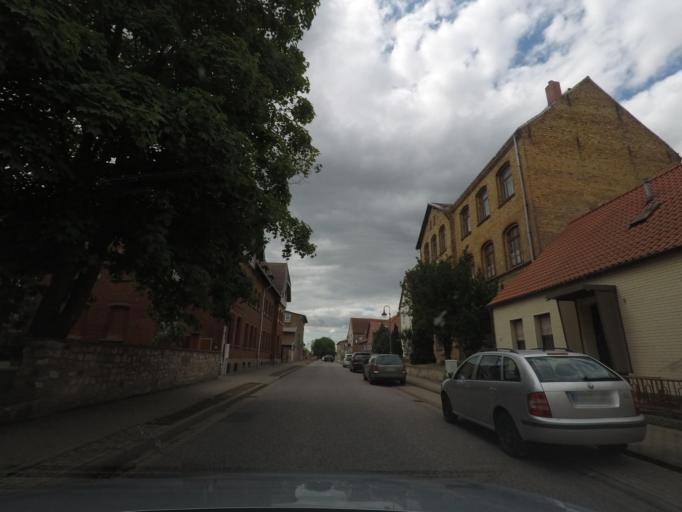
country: DE
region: Saxony-Anhalt
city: Hotensleben
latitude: 52.1202
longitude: 11.0207
